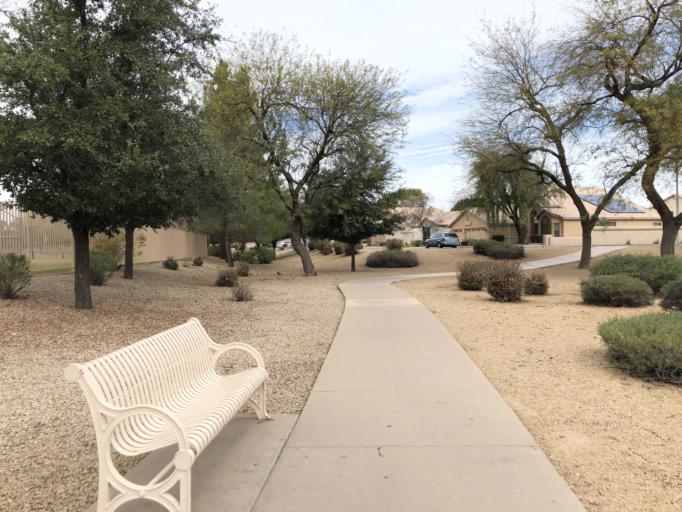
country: US
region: Arizona
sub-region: Maricopa County
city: Guadalupe
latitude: 33.3171
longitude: -111.9164
